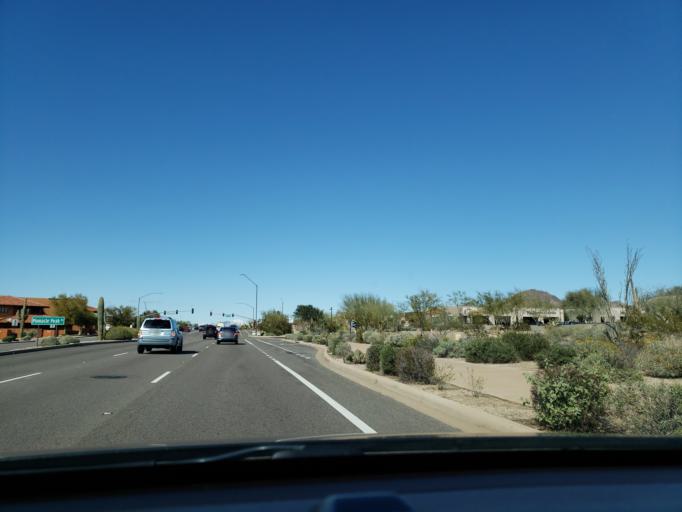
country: US
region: Arizona
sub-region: Maricopa County
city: Carefree
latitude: 33.6969
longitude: -111.8905
